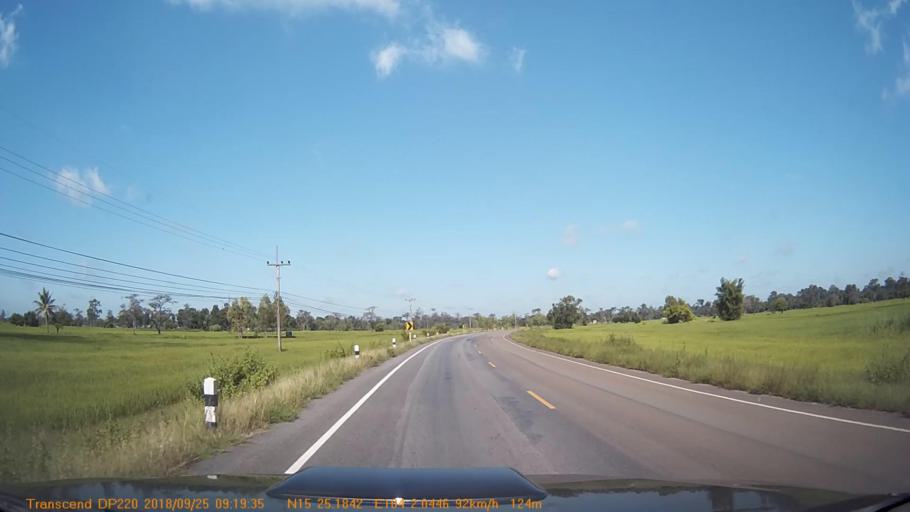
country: TH
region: Sisaket
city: Sila Lat
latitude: 15.4197
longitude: 104.0343
